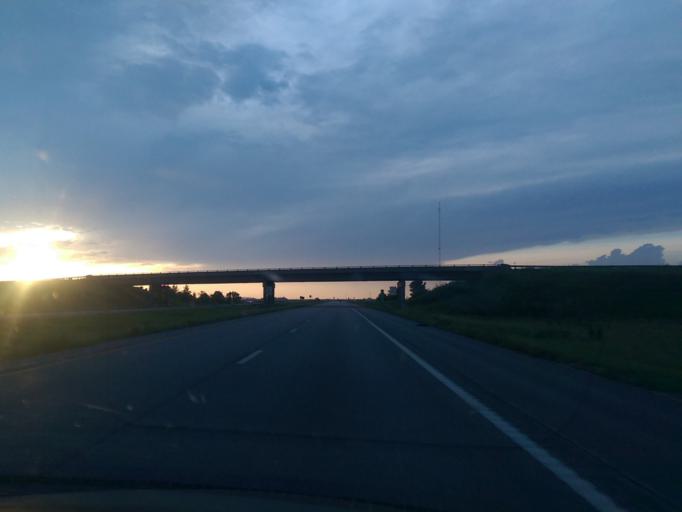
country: US
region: Missouri
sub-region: Atchison County
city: Rock Port
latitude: 40.3680
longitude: -95.5308
